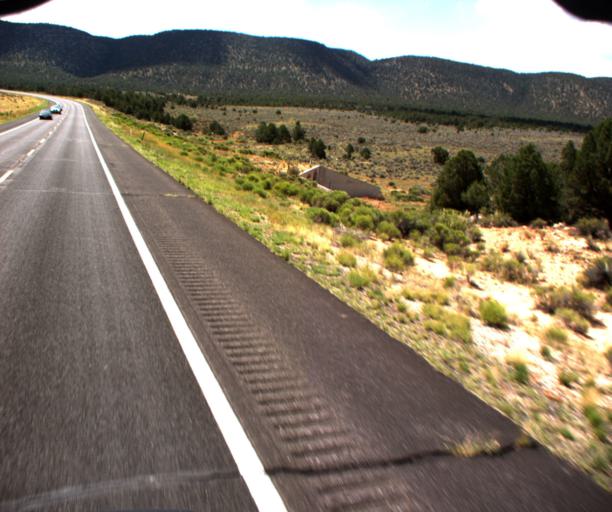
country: US
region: Arizona
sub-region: Coconino County
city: Grand Canyon
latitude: 35.9281
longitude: -111.7648
